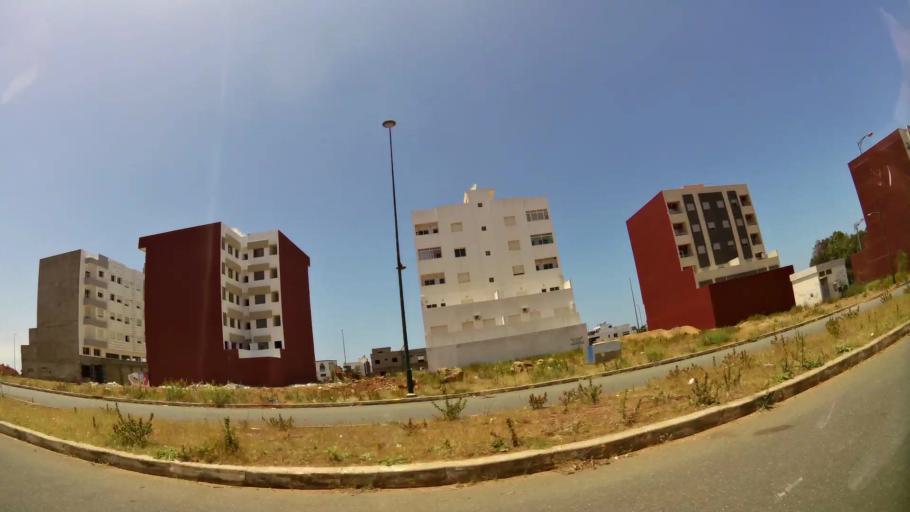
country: MA
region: Gharb-Chrarda-Beni Hssen
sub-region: Kenitra Province
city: Kenitra
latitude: 34.2694
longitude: -6.6274
